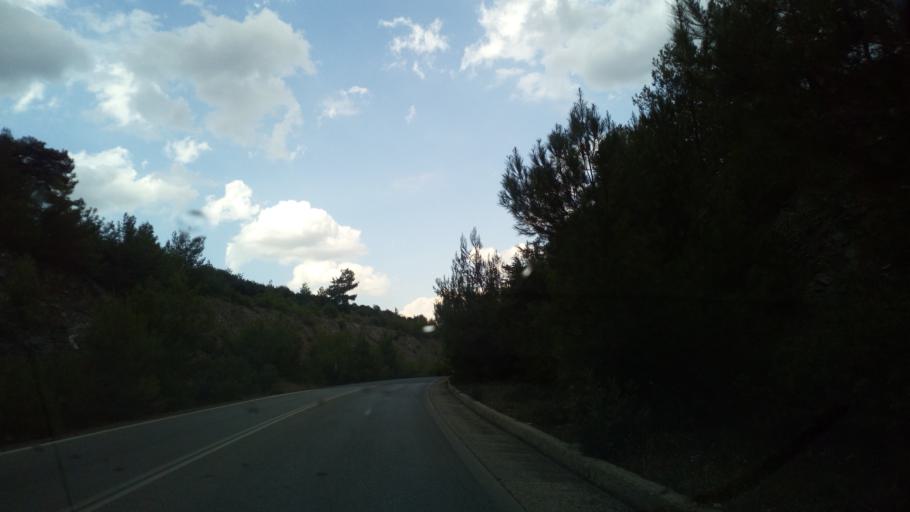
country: GR
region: Central Macedonia
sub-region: Nomos Chalkidikis
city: Polygyros
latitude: 40.3578
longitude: 23.4394
